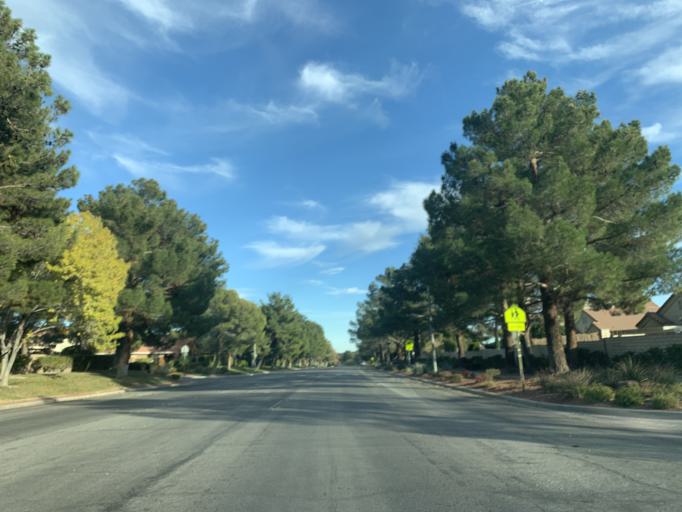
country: US
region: Nevada
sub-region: Clark County
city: Summerlin South
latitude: 36.1333
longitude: -115.2948
